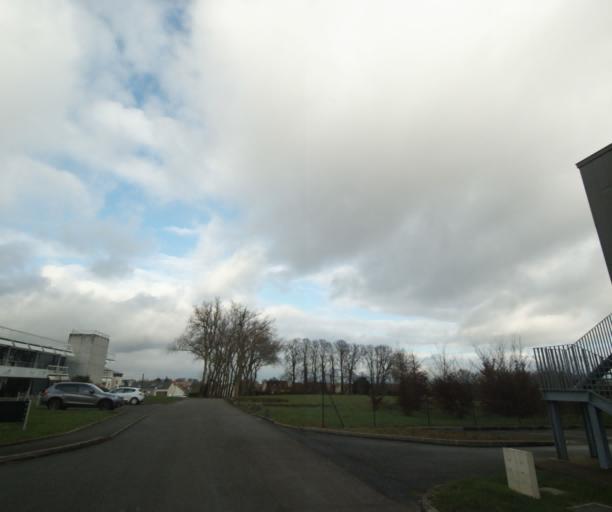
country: FR
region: Pays de la Loire
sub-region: Departement de la Sarthe
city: Rouillon
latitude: 48.0081
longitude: 0.1629
